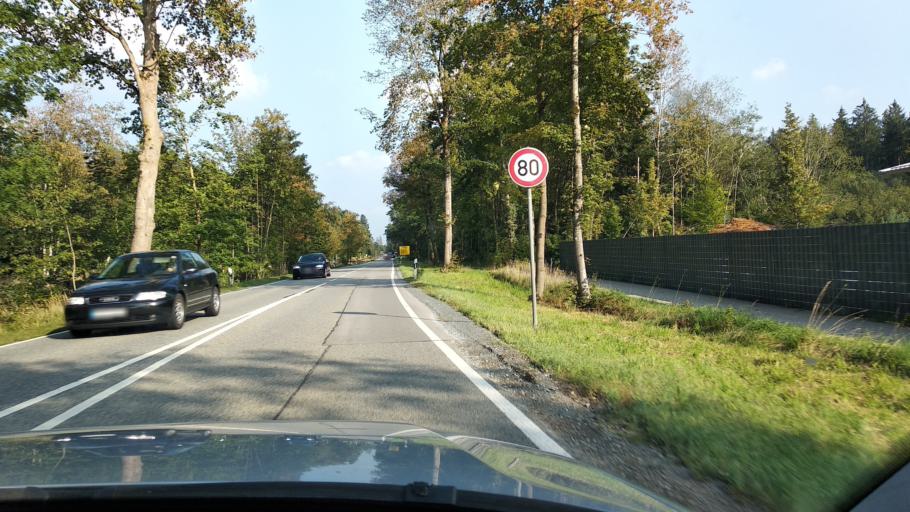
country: DE
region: Bavaria
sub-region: Upper Bavaria
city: Pfaffing
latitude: 48.0794
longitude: 12.0982
